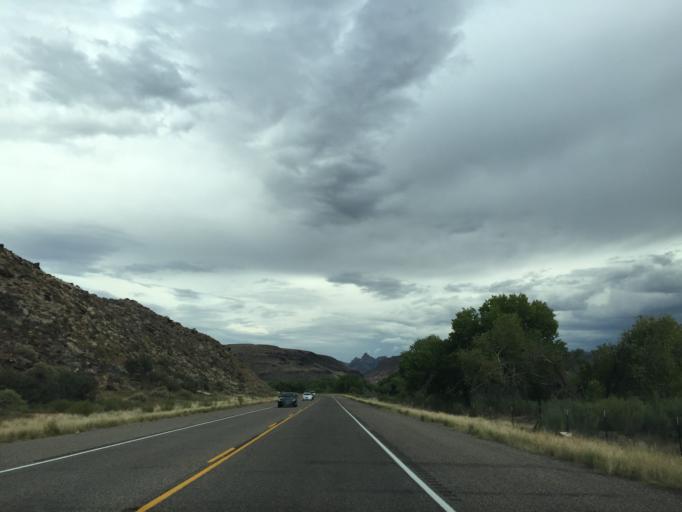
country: US
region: Utah
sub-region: Washington County
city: LaVerkin
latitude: 37.1812
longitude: -113.1295
